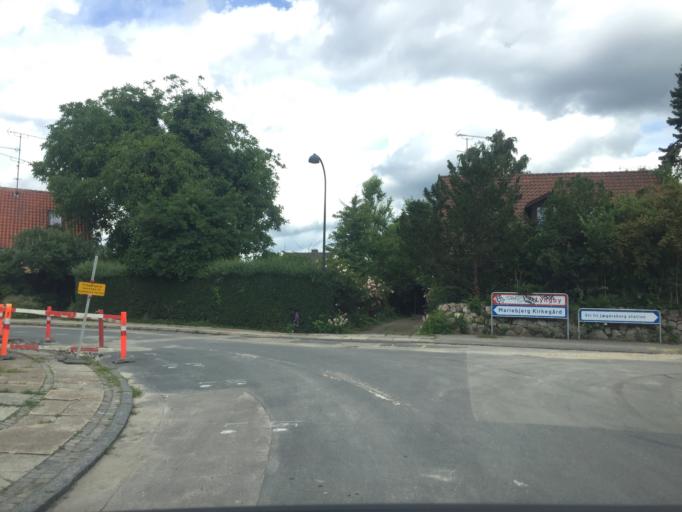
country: DK
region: Capital Region
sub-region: Lyngby-Tarbaek Kommune
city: Kongens Lyngby
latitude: 55.7626
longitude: 12.5165
